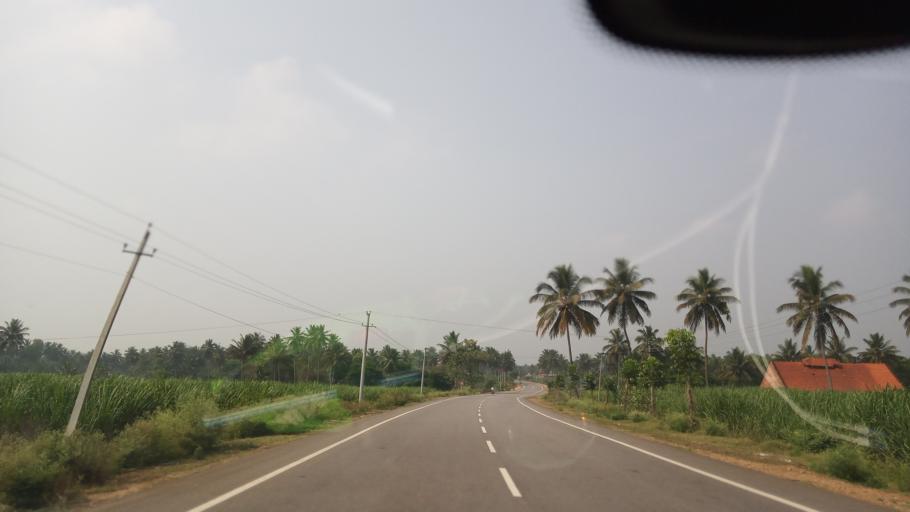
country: IN
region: Karnataka
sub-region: Mandya
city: Pandavapura
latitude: 12.5435
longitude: 76.6708
